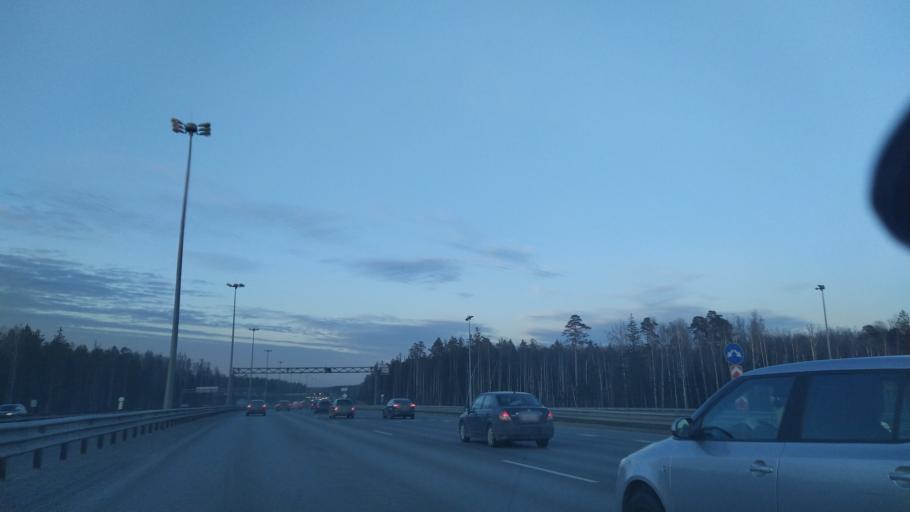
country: RU
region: St.-Petersburg
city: Krasnogvargeisky
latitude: 59.9472
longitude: 30.5418
